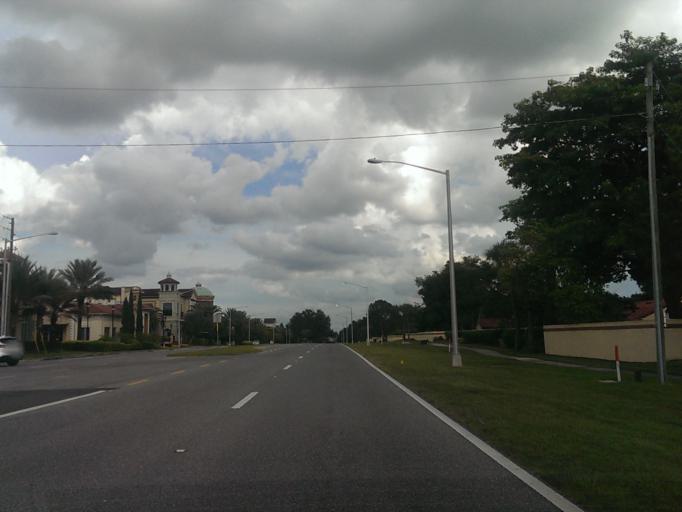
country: US
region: Florida
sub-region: Orange County
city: Doctor Phillips
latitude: 28.4499
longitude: -81.4965
